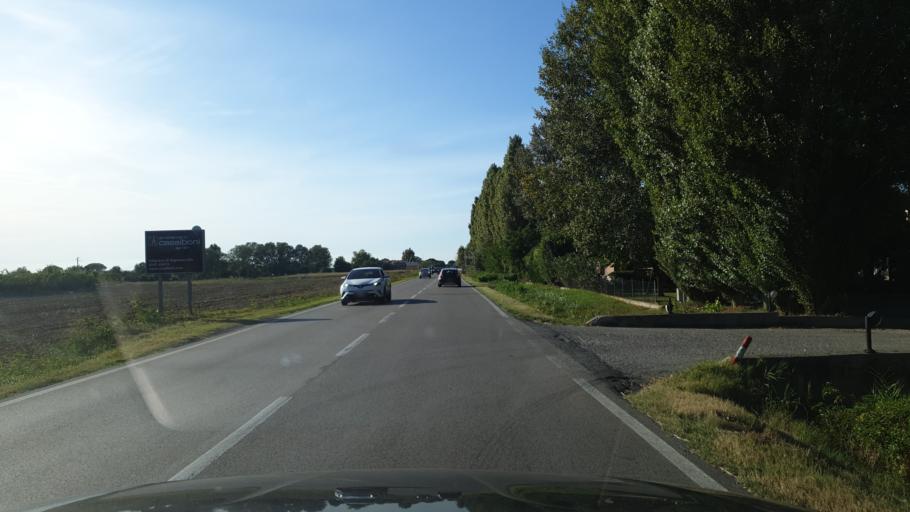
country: IT
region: Emilia-Romagna
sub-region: Provincia di Ravenna
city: Mezzano
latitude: 44.4516
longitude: 12.1157
